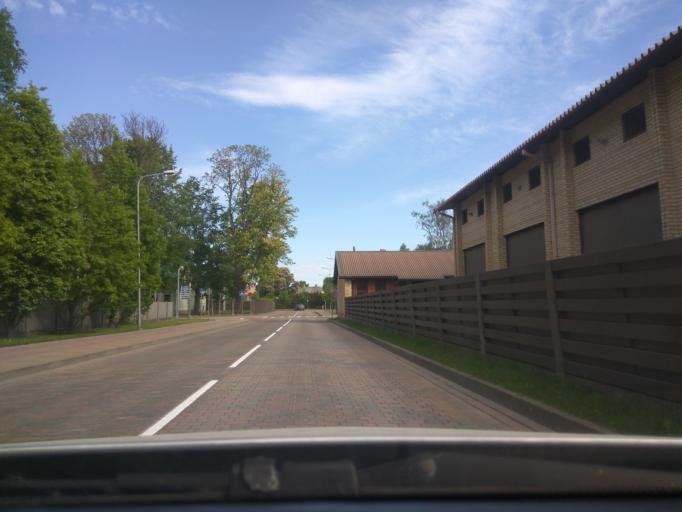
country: LV
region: Ventspils
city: Ventspils
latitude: 57.3966
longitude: 21.5710
